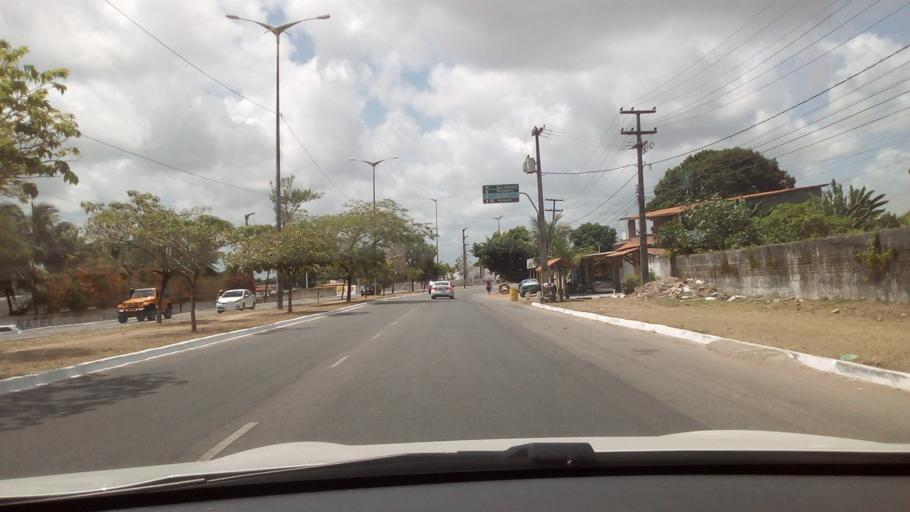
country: BR
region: Paraiba
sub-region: Joao Pessoa
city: Joao Pessoa
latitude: -7.1626
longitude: -34.8240
